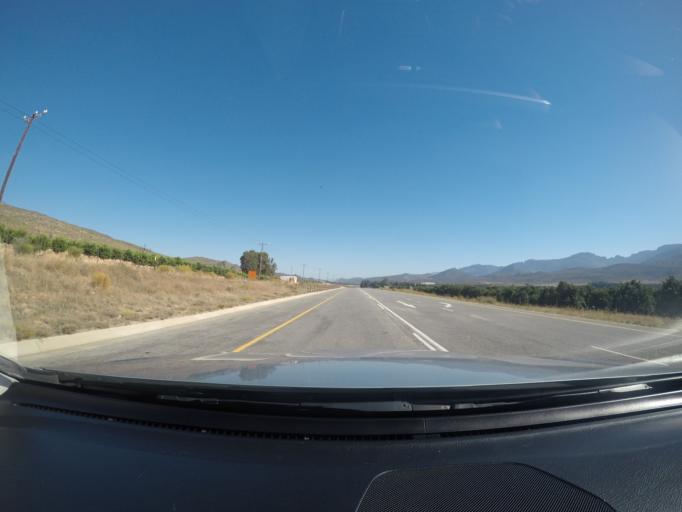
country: ZA
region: Western Cape
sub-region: West Coast District Municipality
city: Clanwilliam
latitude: -32.5061
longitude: 18.9671
